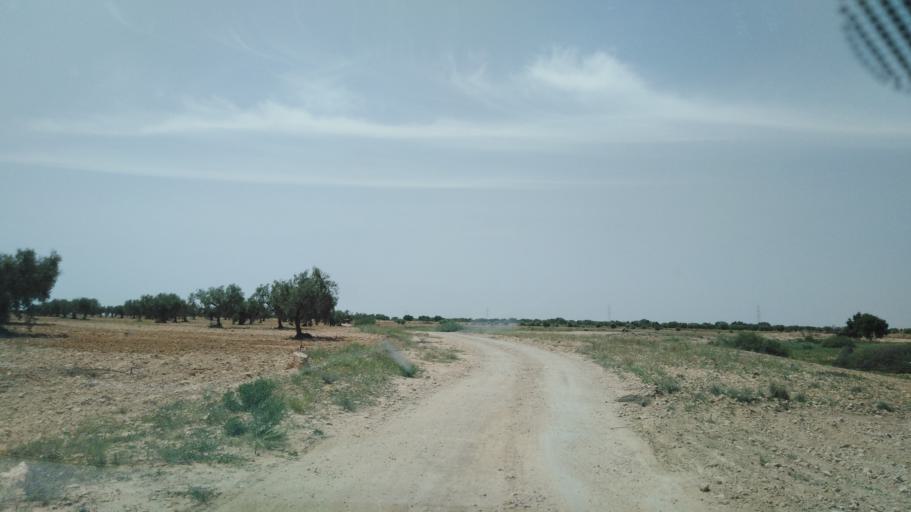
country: TN
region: Safaqis
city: Sfax
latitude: 34.7183
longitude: 10.5676
